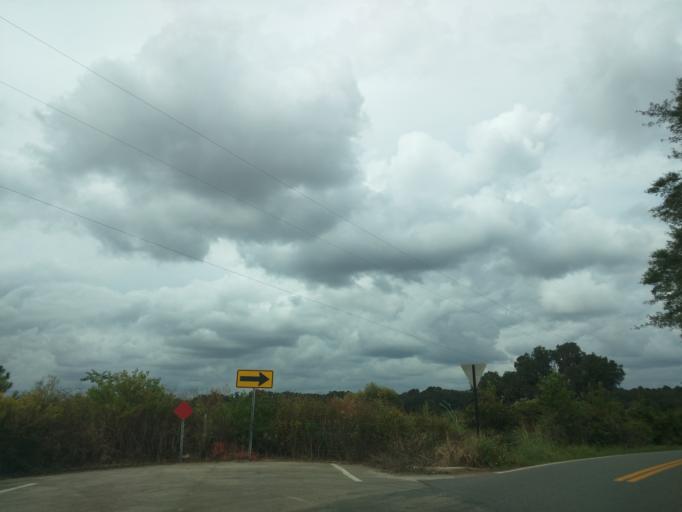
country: US
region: Florida
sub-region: Leon County
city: Tallahassee
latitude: 30.4059
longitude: -84.2104
